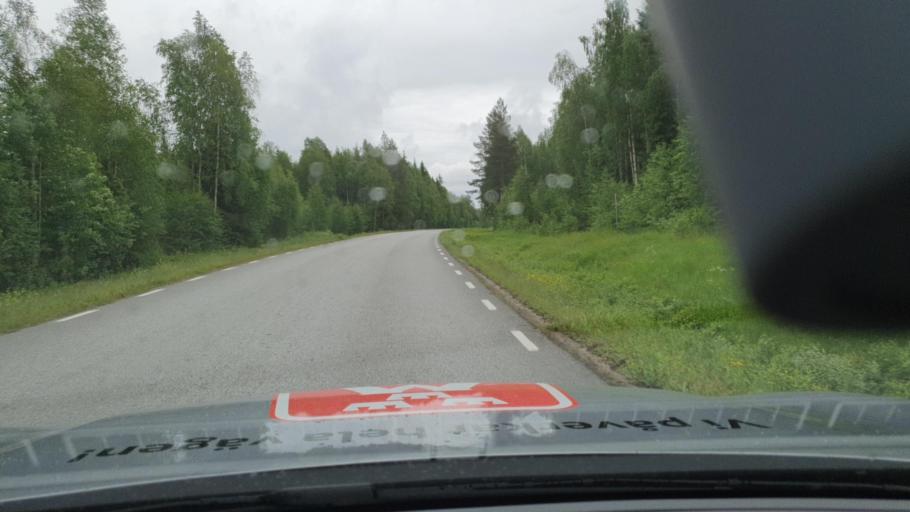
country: SE
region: Norrbotten
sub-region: Kalix Kommun
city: Toere
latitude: 65.8896
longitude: 22.6490
